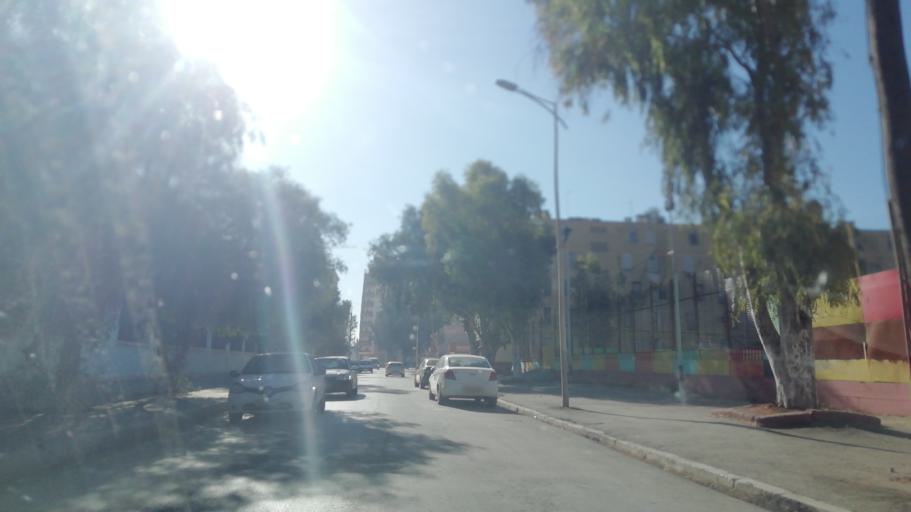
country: DZ
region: Oran
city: Oran
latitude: 35.6689
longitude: -0.6493
